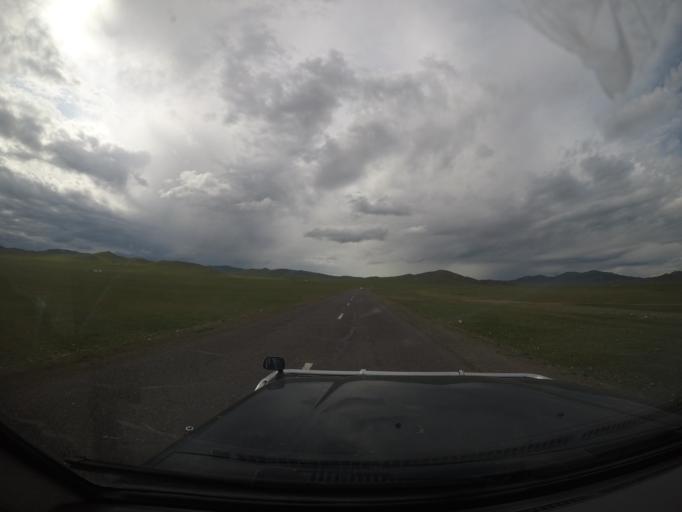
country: MN
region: Hentiy
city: Modot
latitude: 47.6598
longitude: 109.1309
